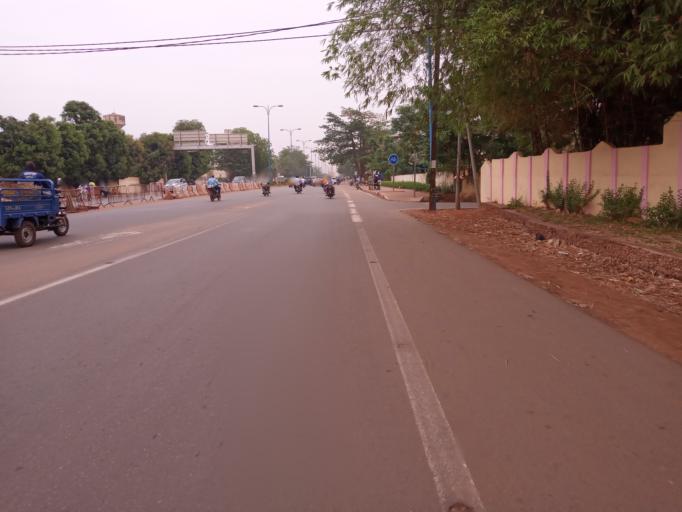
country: ML
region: Bamako
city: Bamako
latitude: 12.6332
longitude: -8.0086
